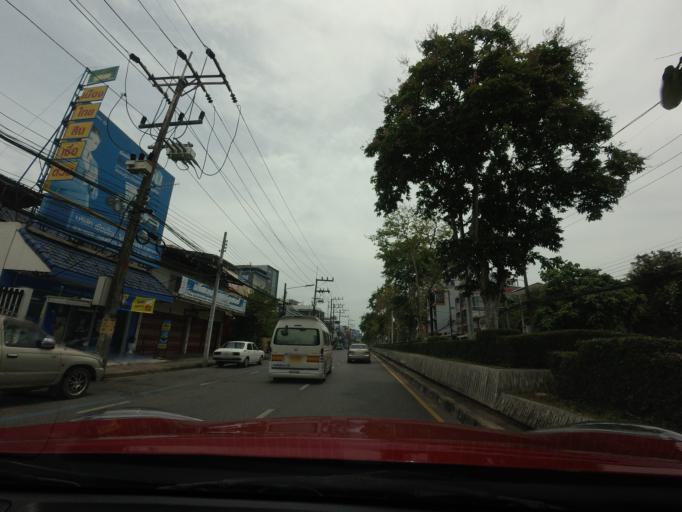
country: TH
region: Songkhla
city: Hat Yai
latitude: 6.9987
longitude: 100.4881
